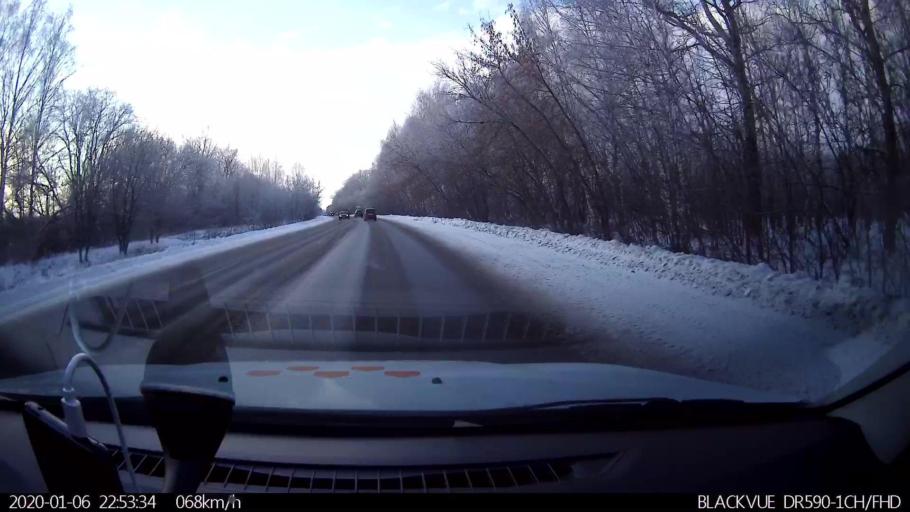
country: RU
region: Nizjnij Novgorod
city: Bogorodsk
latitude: 56.1237
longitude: 43.5634
